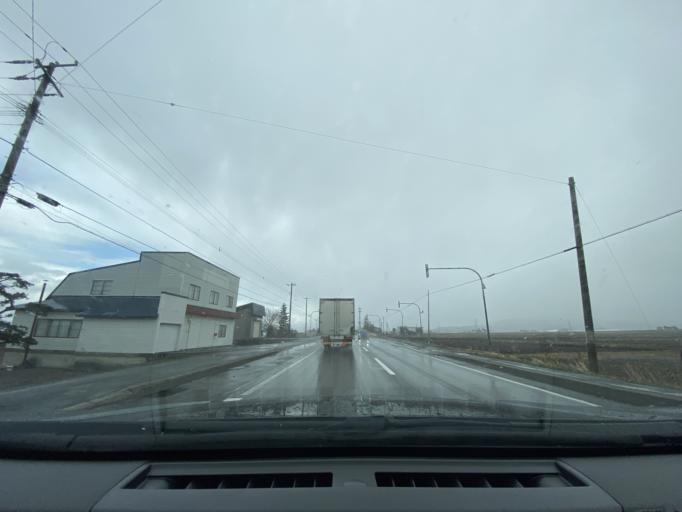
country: JP
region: Hokkaido
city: Fukagawa
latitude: 43.6581
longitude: 141.9858
